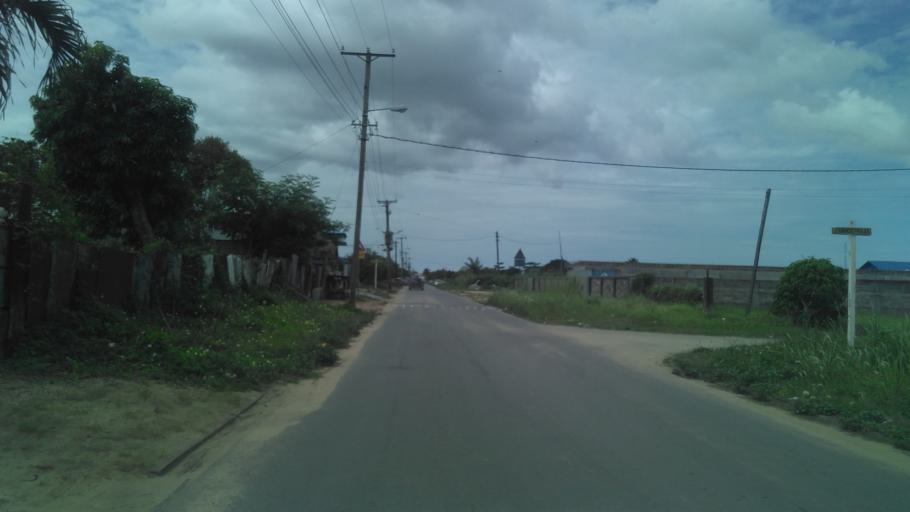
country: SR
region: Paramaribo
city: Paramaribo
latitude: 5.8466
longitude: -55.1231
